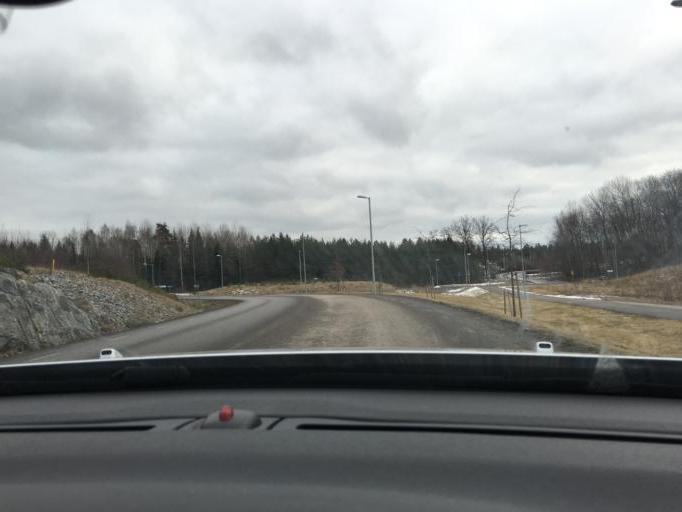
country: SE
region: Soedermanland
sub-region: Katrineholms Kommun
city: Katrineholm
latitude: 58.9954
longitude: 16.2425
